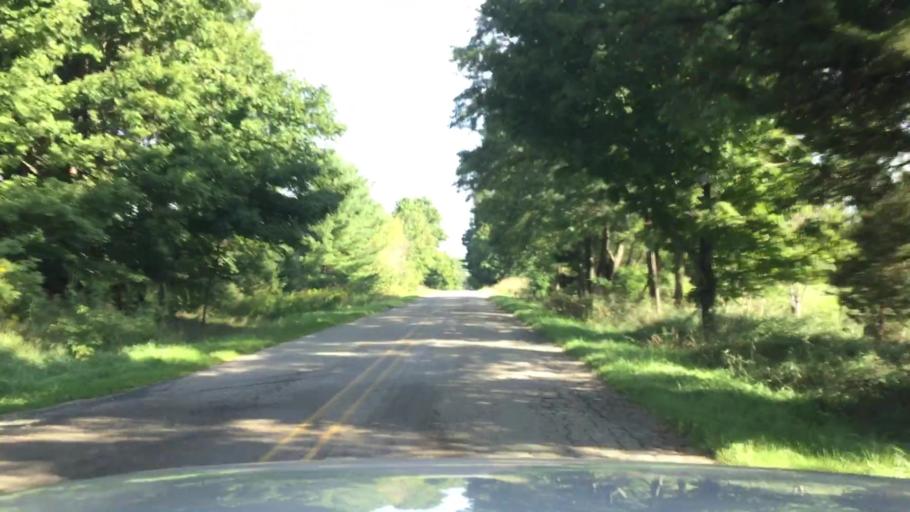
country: US
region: Michigan
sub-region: Lenawee County
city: Hudson
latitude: 41.8750
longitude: -84.4201
